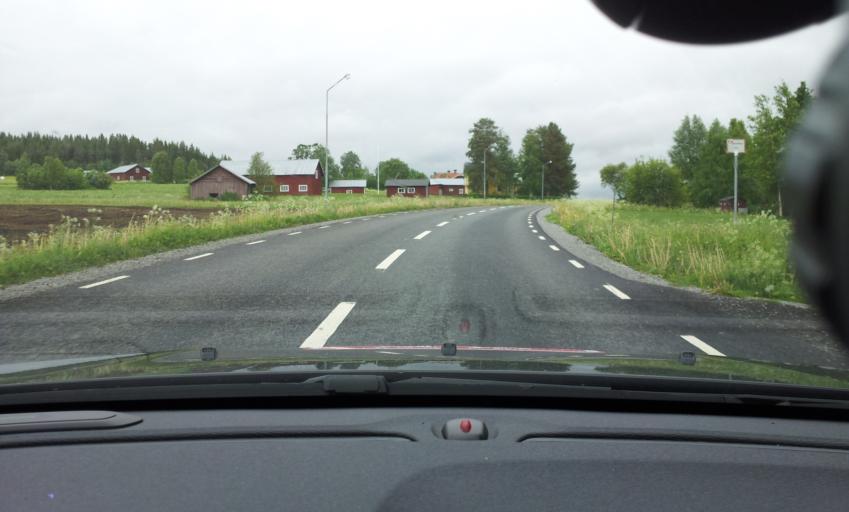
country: SE
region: Jaemtland
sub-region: OEstersunds Kommun
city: Lit
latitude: 63.7396
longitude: 14.8595
